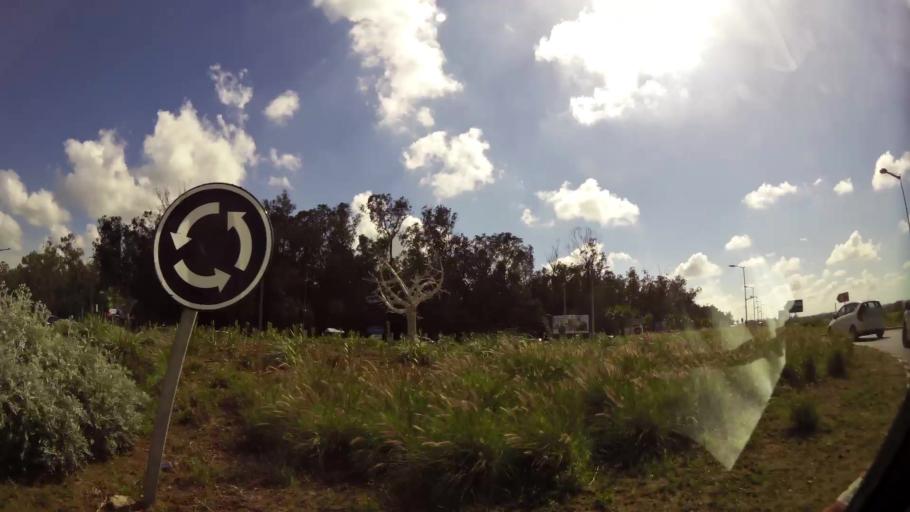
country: MA
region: Grand Casablanca
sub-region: Nouaceur
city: Bouskoura
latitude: 33.4830
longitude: -7.6257
